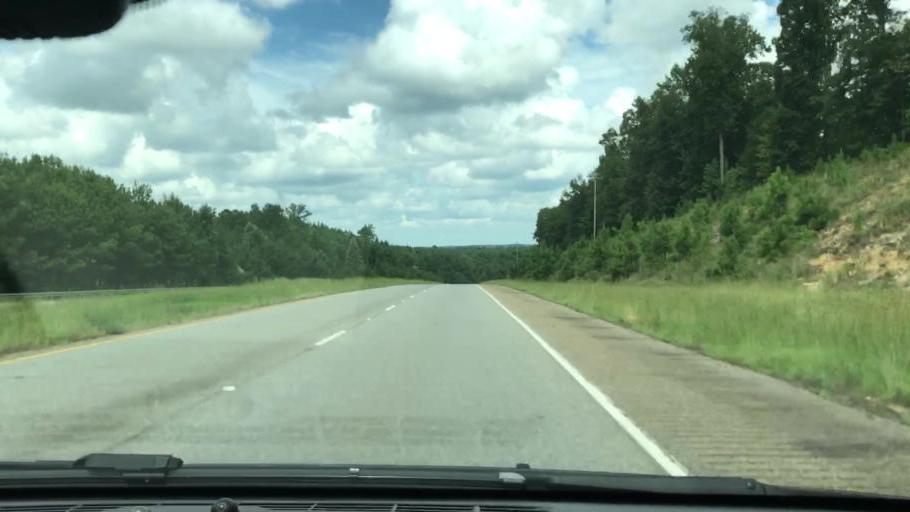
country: US
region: Georgia
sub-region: Stewart County
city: Lumpkin
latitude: 32.1224
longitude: -84.8194
